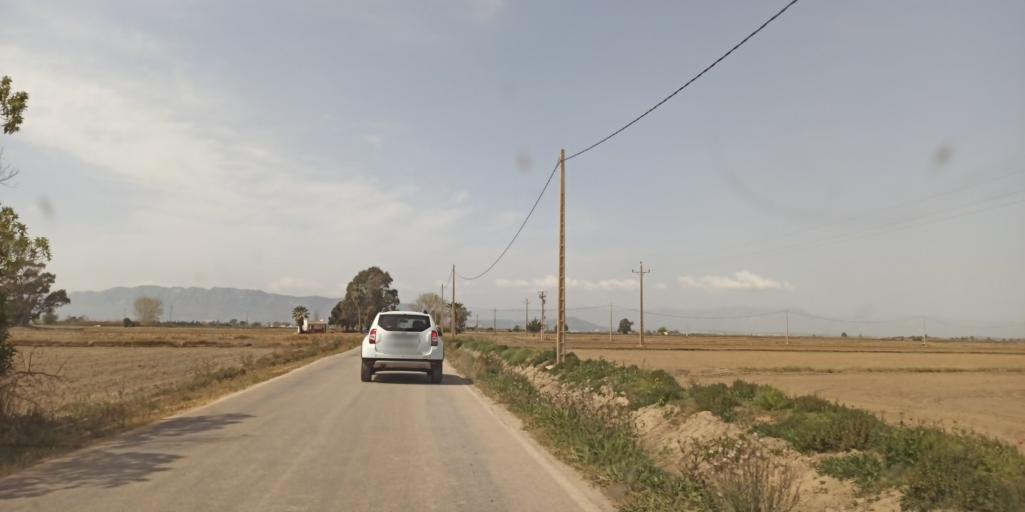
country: ES
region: Catalonia
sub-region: Provincia de Tarragona
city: Deltebre
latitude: 40.6462
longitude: 0.7158
